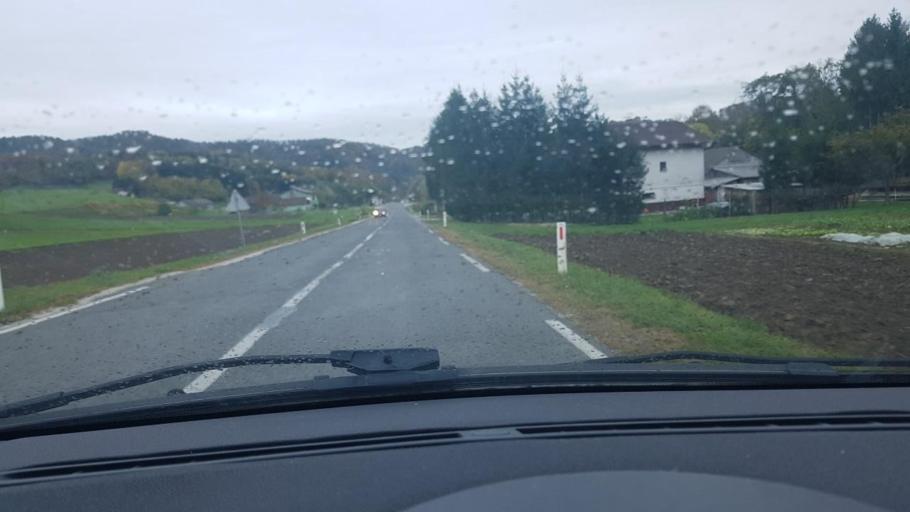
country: SI
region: Rogatec
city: Rogatec
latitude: 46.2456
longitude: 15.7008
